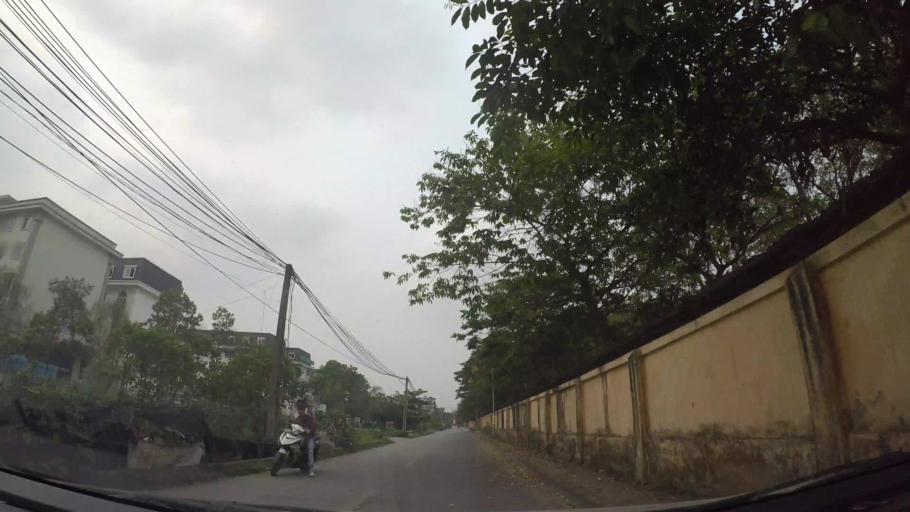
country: VN
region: Ha Noi
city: Cau Dien
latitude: 21.0405
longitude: 105.7512
